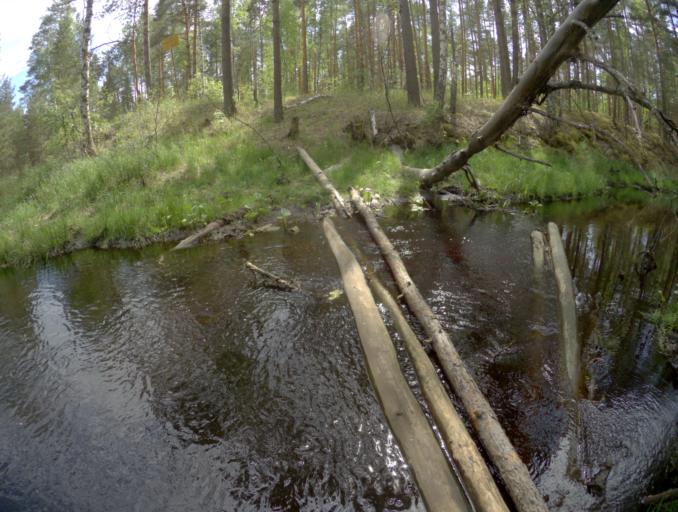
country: RU
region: Vladimir
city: Ivanishchi
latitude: 55.6971
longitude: 40.4276
